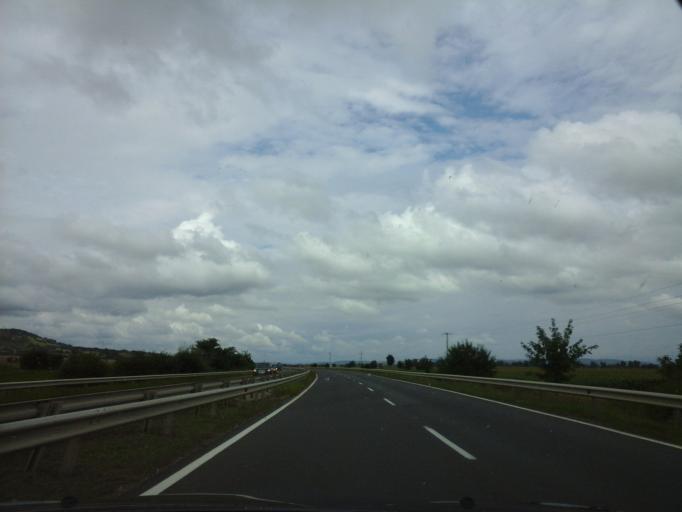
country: HU
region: Borsod-Abauj-Zemplen
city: Sajobabony
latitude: 48.1950
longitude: 20.7478
